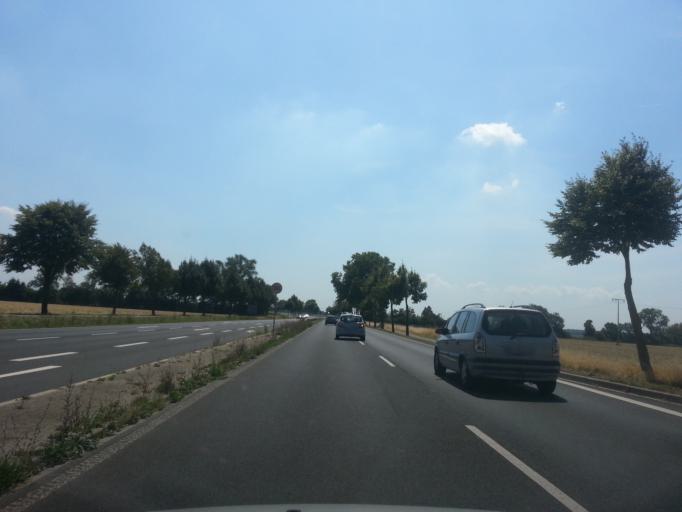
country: DE
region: Hesse
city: Lampertheim
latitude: 49.5810
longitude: 8.4478
